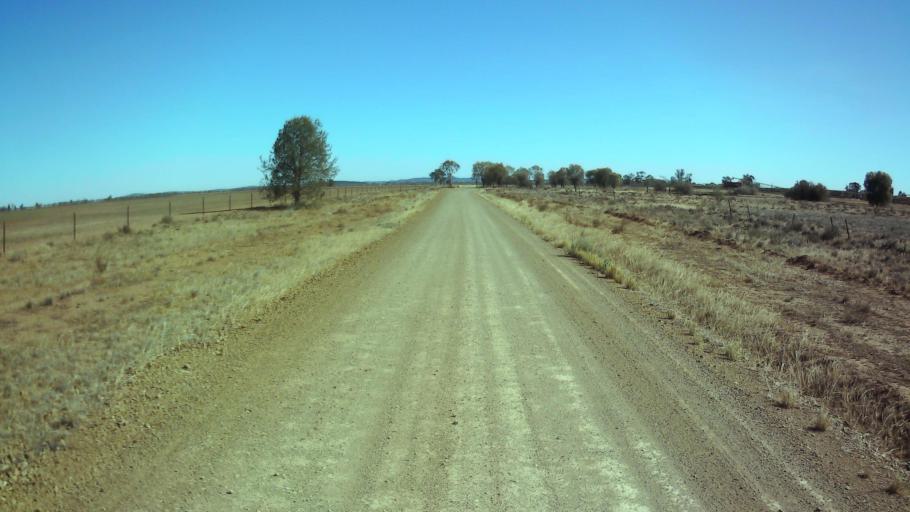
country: AU
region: New South Wales
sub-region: Weddin
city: Grenfell
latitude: -33.8381
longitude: 147.7416
